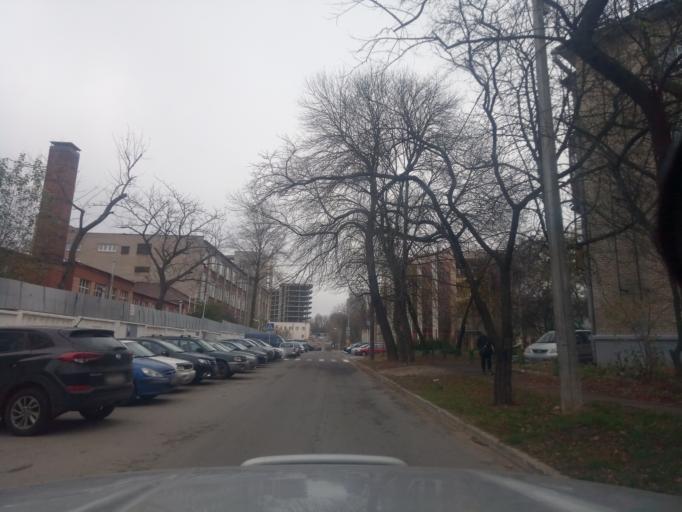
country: BY
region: Minsk
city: Minsk
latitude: 53.8985
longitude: 27.5385
